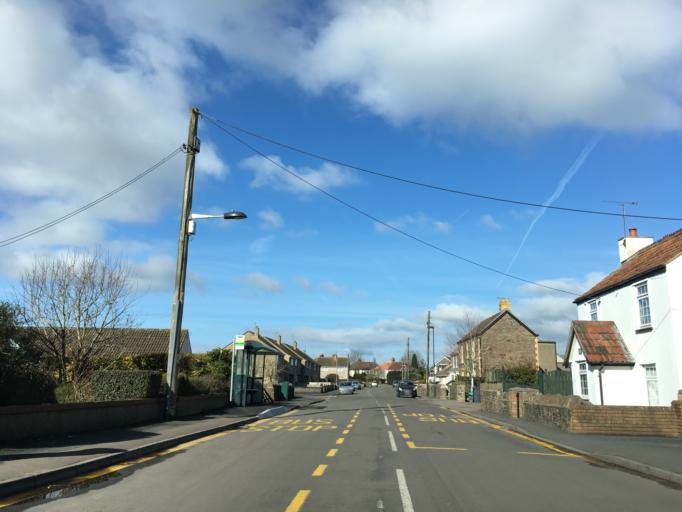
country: GB
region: England
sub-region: South Gloucestershire
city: Winterbourne
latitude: 51.5294
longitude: -2.4975
